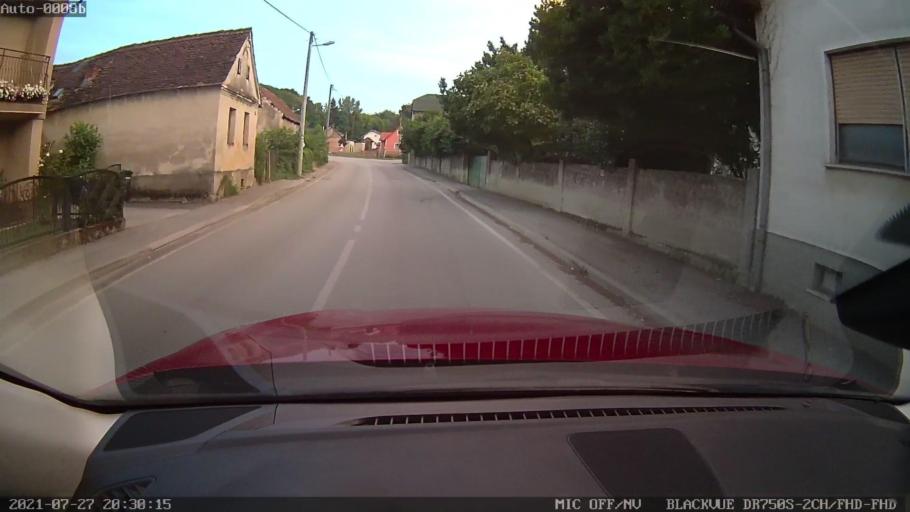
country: HR
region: Varazdinska
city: Jalzabet
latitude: 46.2562
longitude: 16.4730
